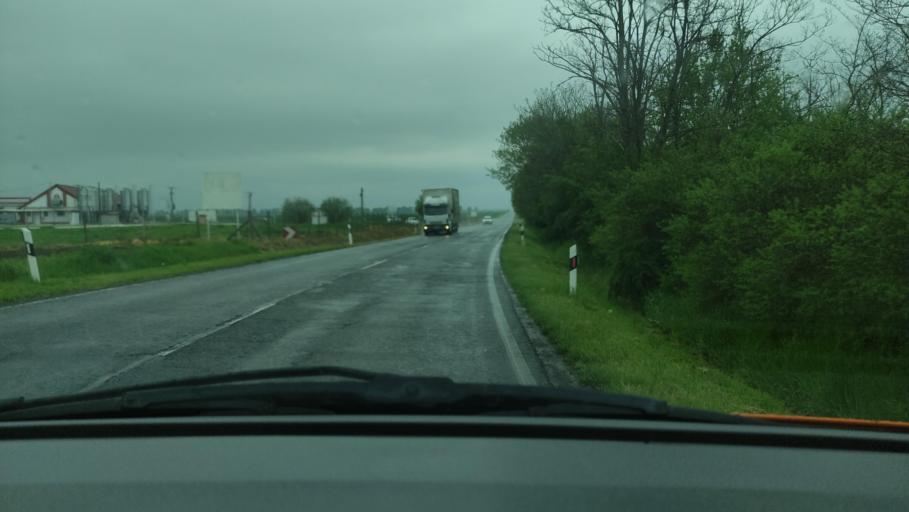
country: HU
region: Baranya
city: Mohacs
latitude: 45.9276
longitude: 18.6596
